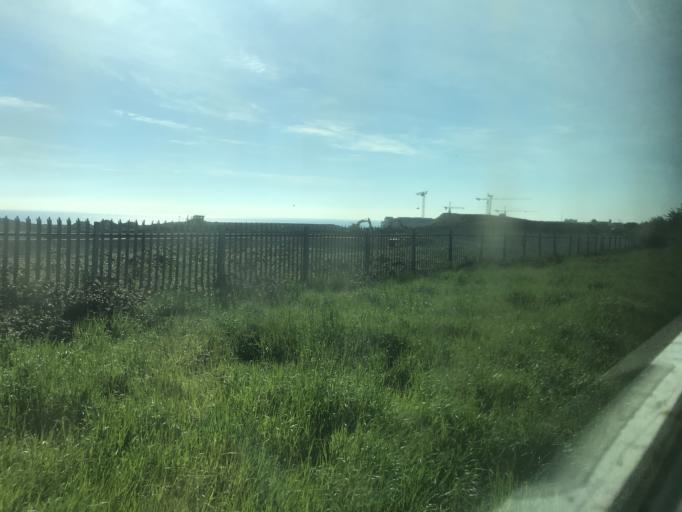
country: IE
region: Leinster
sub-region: Wicklow
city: Greystones
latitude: 53.1566
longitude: -6.0755
